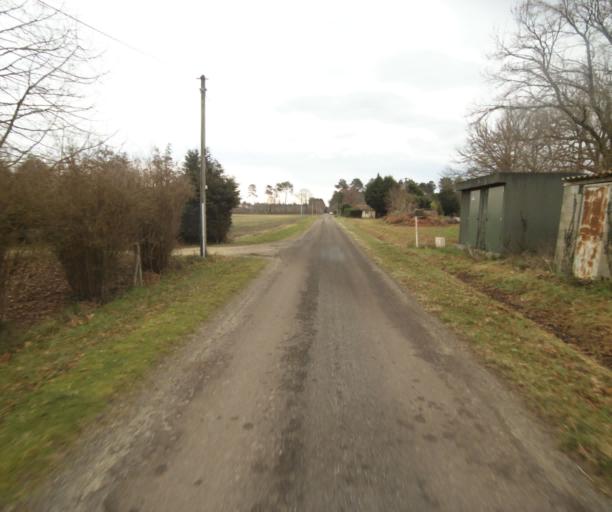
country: FR
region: Midi-Pyrenees
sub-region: Departement du Gers
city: Cazaubon
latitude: 44.0215
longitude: -0.0784
